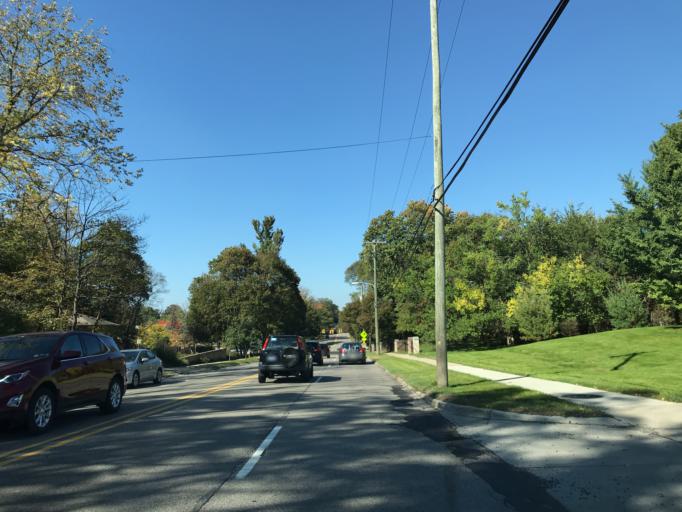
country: US
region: Michigan
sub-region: Washtenaw County
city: Ann Arbor
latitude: 42.2661
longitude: -83.7200
